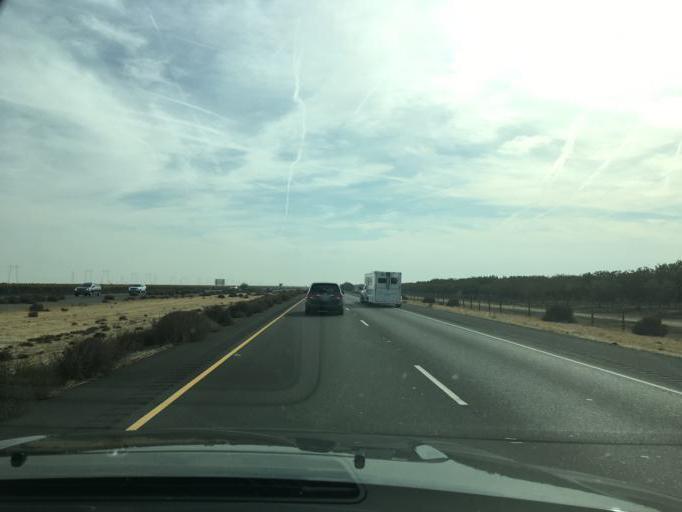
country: US
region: California
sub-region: Kings County
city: Kettleman City
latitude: 35.9224
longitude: -119.8998
